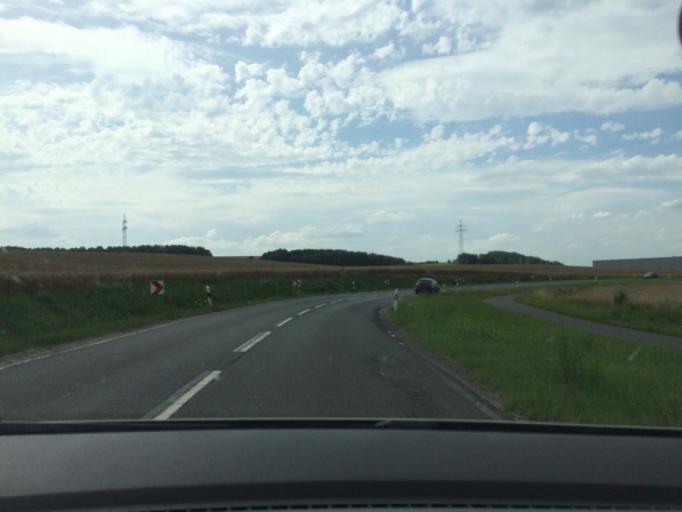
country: DE
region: Bavaria
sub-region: Regierungsbezirk Unterfranken
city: Sailauf
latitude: 49.9908
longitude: 9.2496
